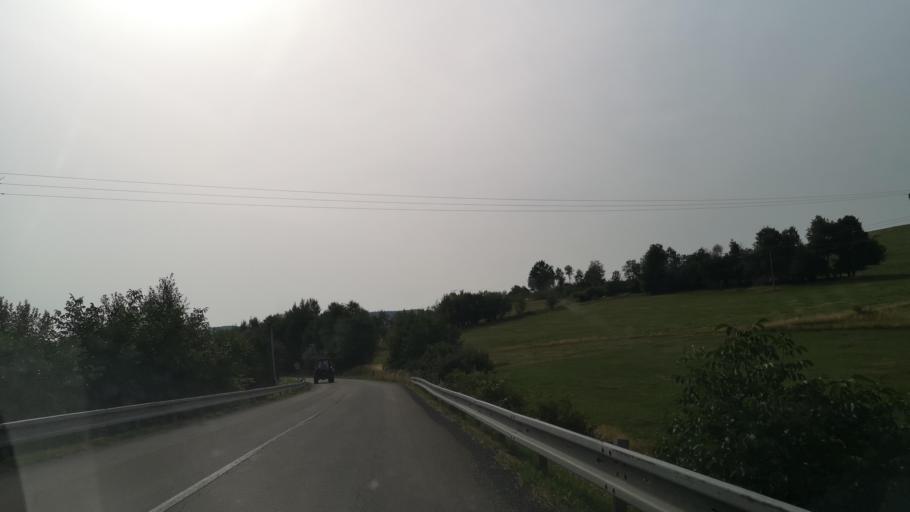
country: SK
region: Banskobystricky
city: Poltar
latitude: 48.5922
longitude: 19.7354
